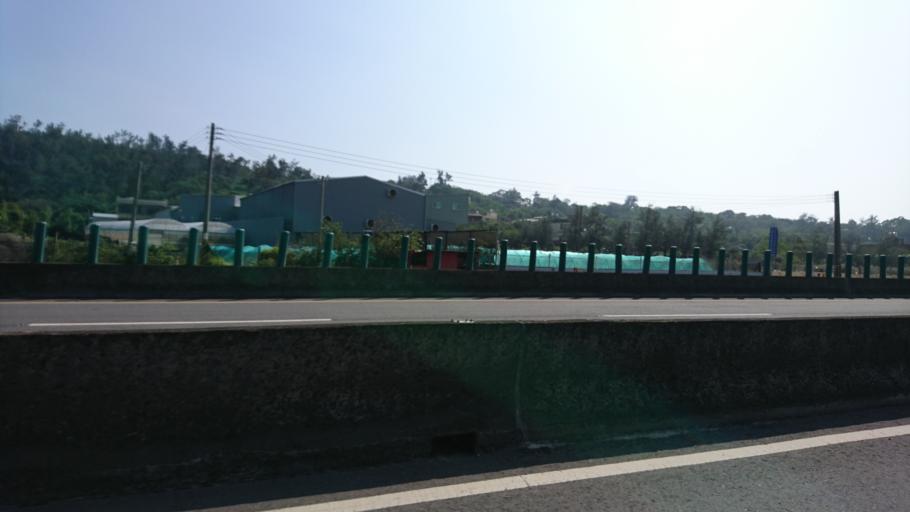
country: TW
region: Taiwan
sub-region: Hsinchu
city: Hsinchu
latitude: 24.7333
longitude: 120.8804
